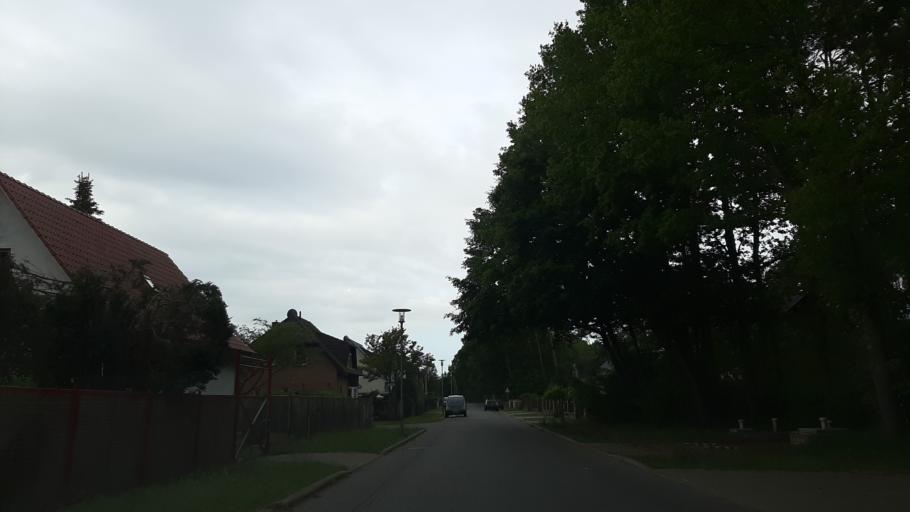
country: DE
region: Brandenburg
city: Hennigsdorf
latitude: 52.6480
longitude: 13.1892
